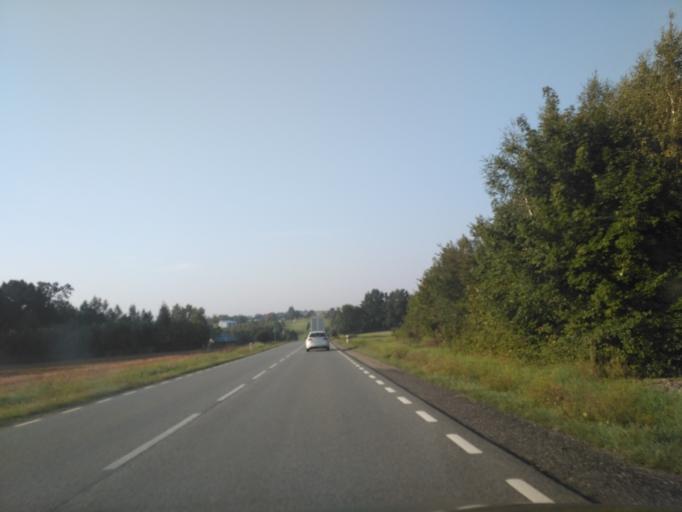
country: PL
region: Lublin Voivodeship
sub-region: Powiat janowski
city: Modliborzyce
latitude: 50.8024
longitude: 22.3194
